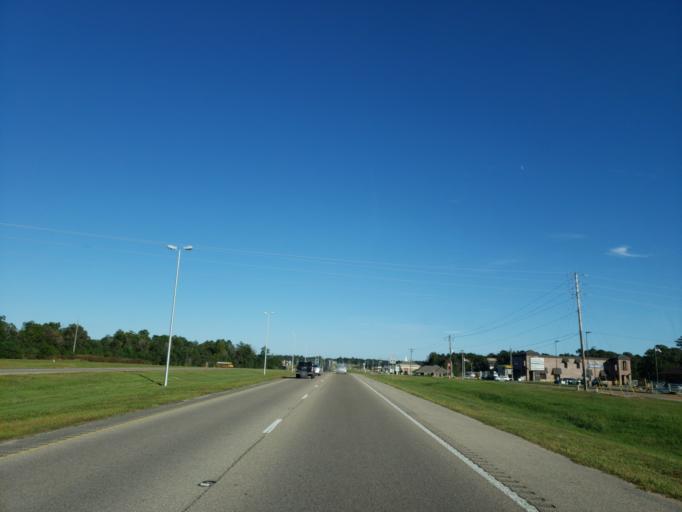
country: US
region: Mississippi
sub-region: Forrest County
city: Petal
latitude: 31.3521
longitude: -89.2466
